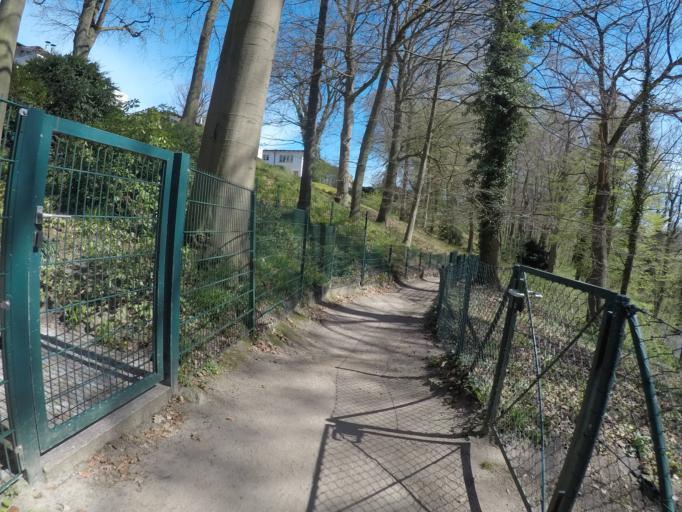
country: DE
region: Hamburg
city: Lemsahl-Mellingstedt
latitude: 53.6729
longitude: 10.0949
